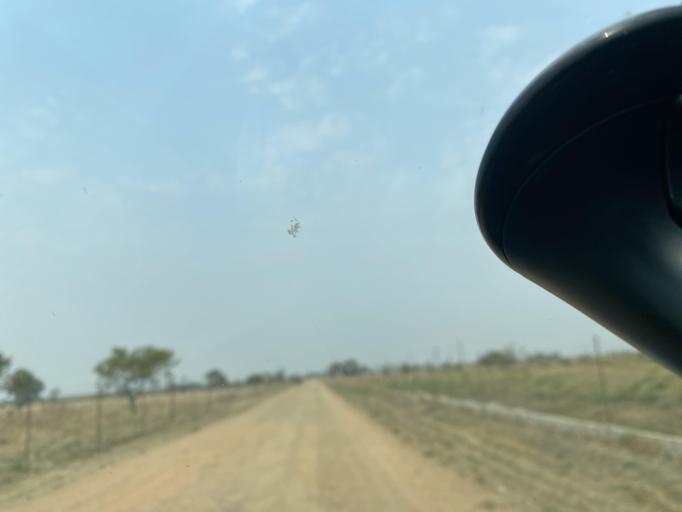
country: ZM
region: Lusaka
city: Kafue
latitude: -15.6820
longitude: 28.0106
